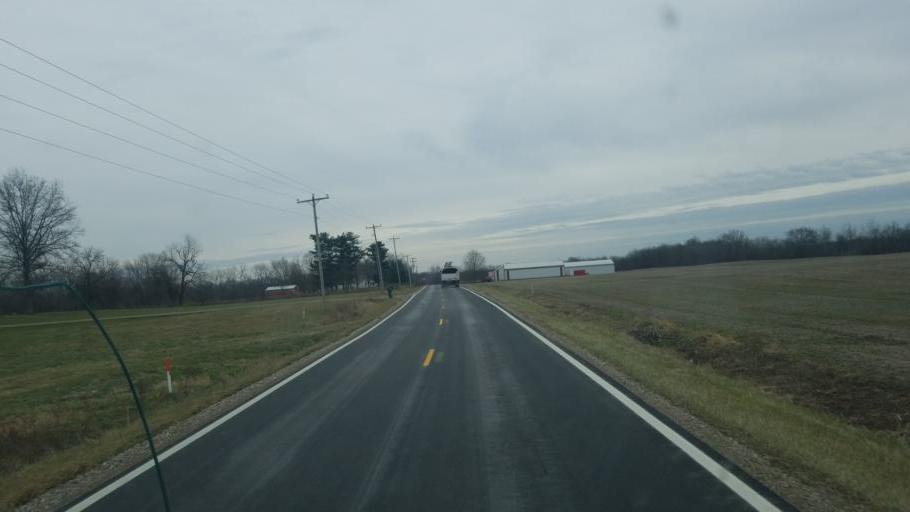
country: US
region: Ohio
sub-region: Licking County
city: Utica
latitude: 40.2552
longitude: -82.5487
